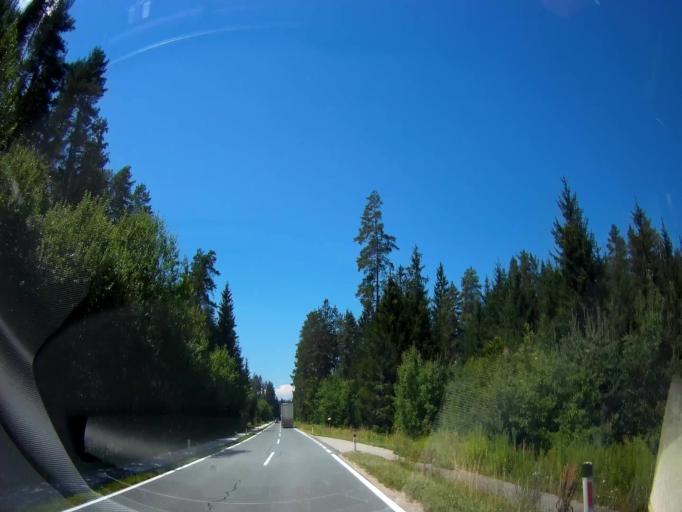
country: AT
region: Carinthia
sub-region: Politischer Bezirk Volkermarkt
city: Eberndorf
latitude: 46.6145
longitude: 14.6629
